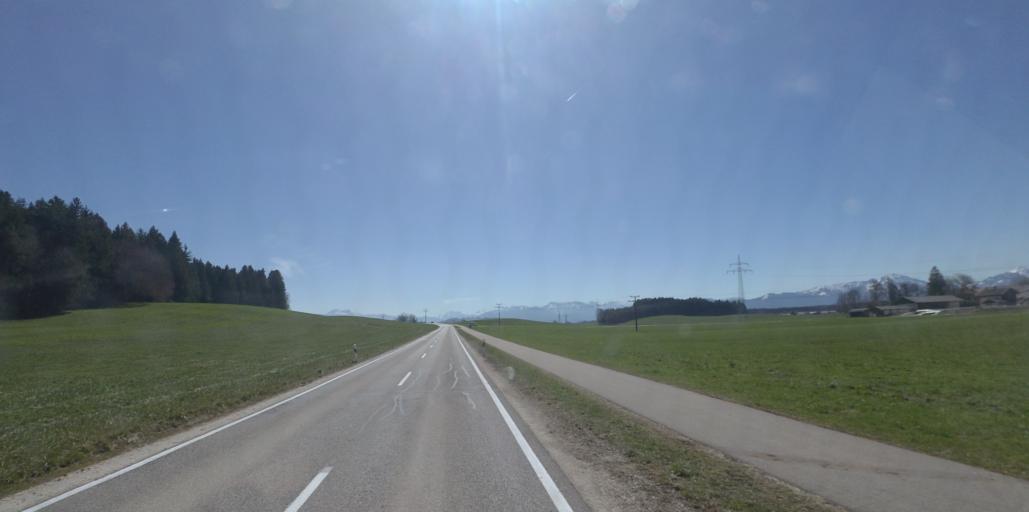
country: DE
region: Bavaria
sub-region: Upper Bavaria
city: Nussdorf
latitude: 47.8909
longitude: 12.6124
